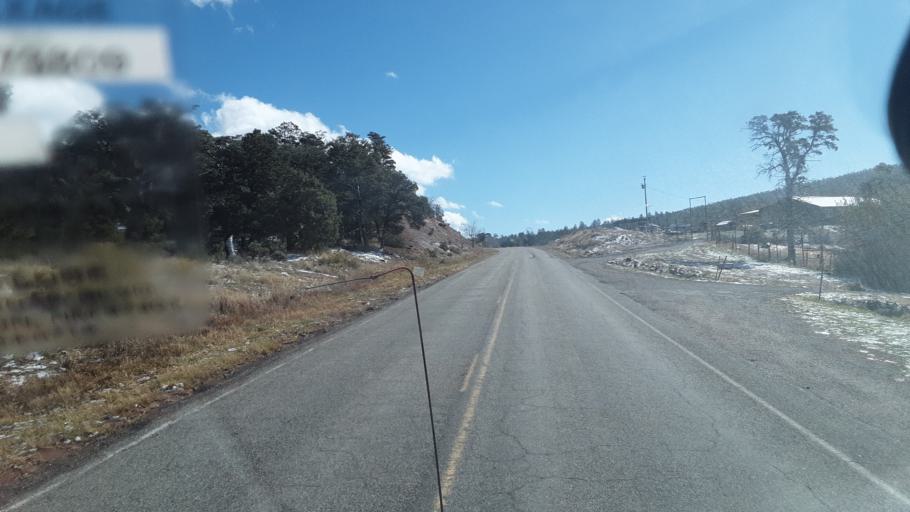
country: US
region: New Mexico
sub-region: Rio Arriba County
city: Santa Teresa
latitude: 36.2303
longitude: -106.8291
